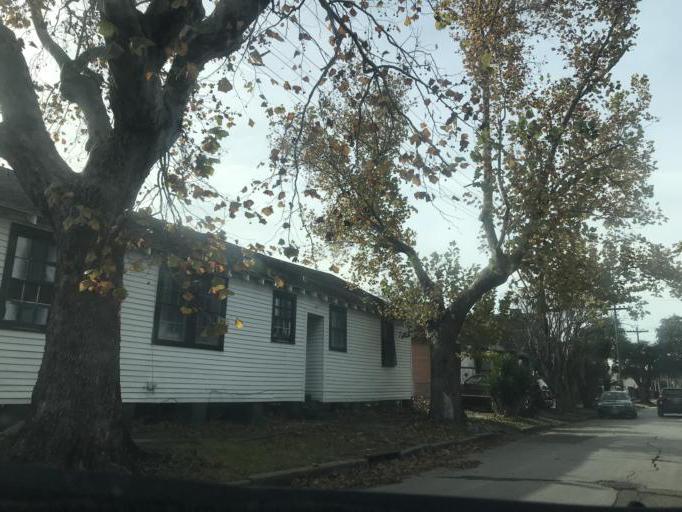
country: US
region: Louisiana
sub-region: Orleans Parish
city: New Orleans
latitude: 29.9590
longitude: -90.1127
